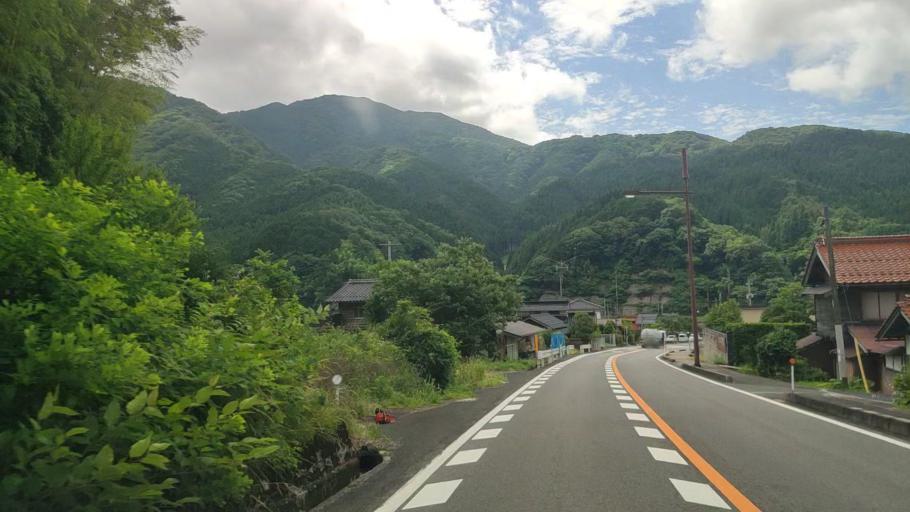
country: JP
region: Tottori
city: Yonago
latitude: 35.2463
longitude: 133.4444
